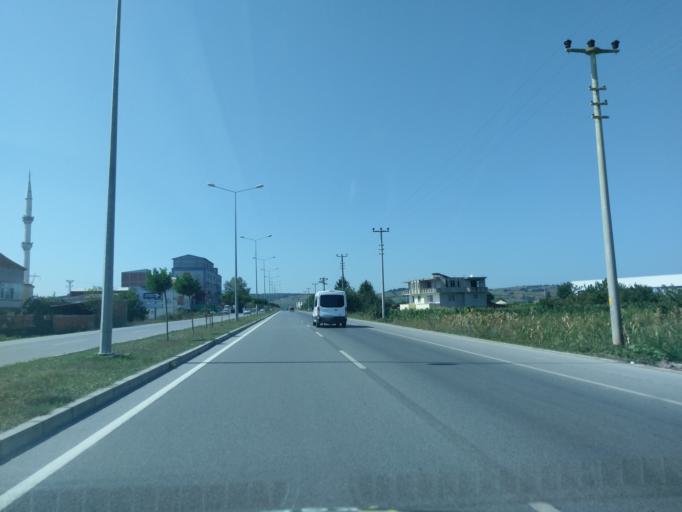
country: TR
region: Samsun
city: Bafra
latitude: 41.5728
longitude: 35.8686
